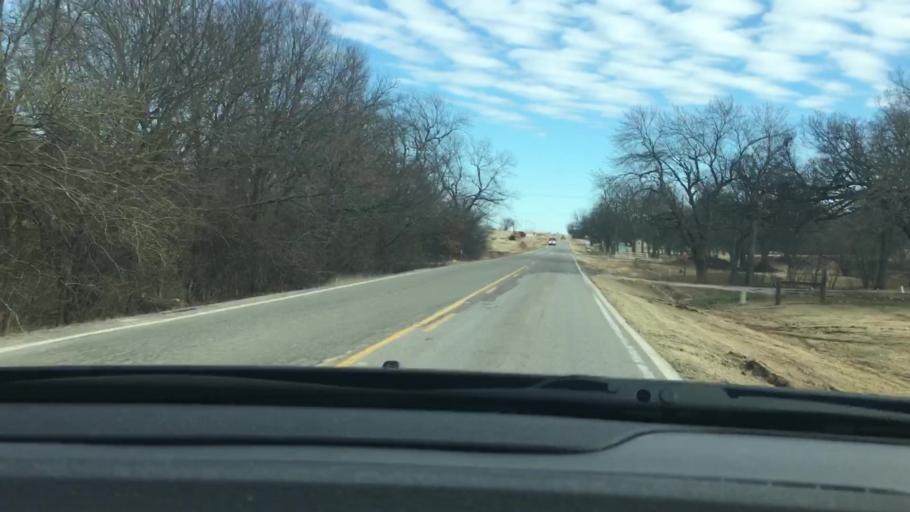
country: US
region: Oklahoma
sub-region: Garvin County
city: Stratford
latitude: 34.7966
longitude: -96.9339
